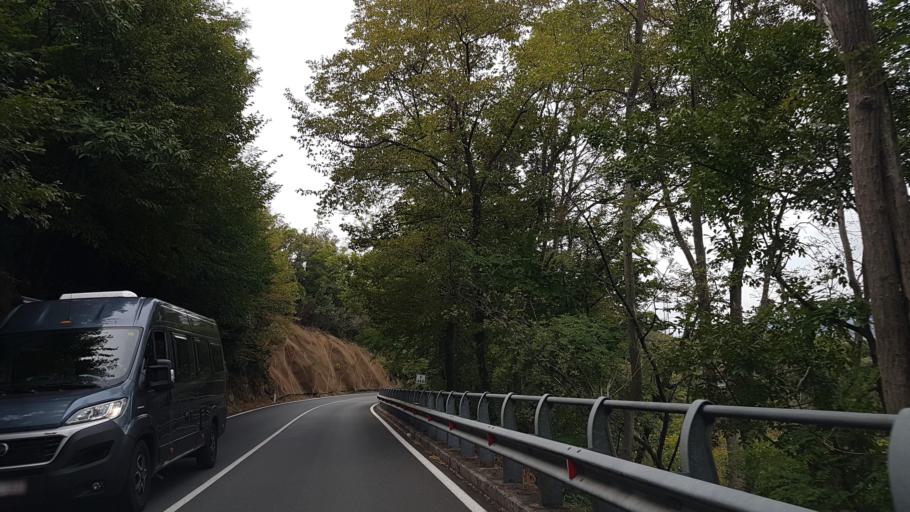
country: IT
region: Liguria
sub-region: Provincia di Genova
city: Casarza Ligure
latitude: 44.2617
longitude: 9.4488
